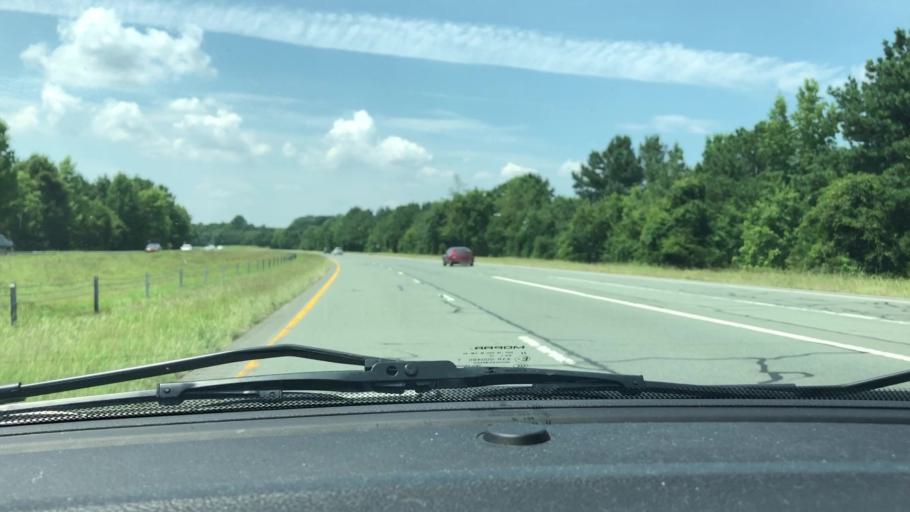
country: US
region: North Carolina
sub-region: Chatham County
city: Siler City
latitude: 35.7386
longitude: -79.4335
